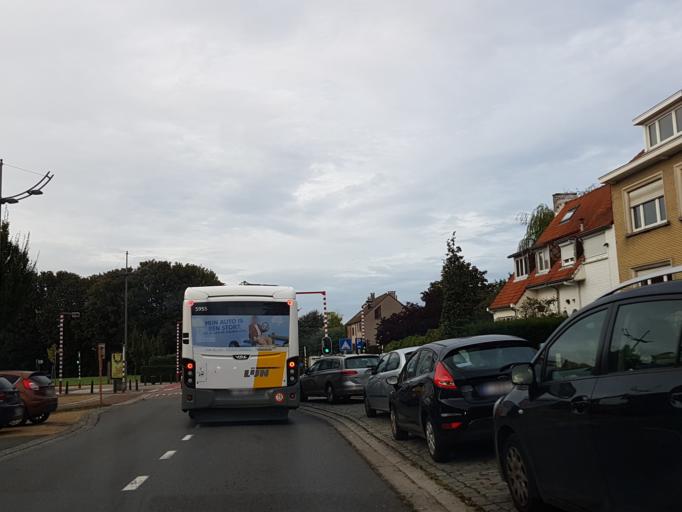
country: BE
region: Flanders
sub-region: Provincie Vlaams-Brabant
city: Kraainem
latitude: 50.8554
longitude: 4.4649
